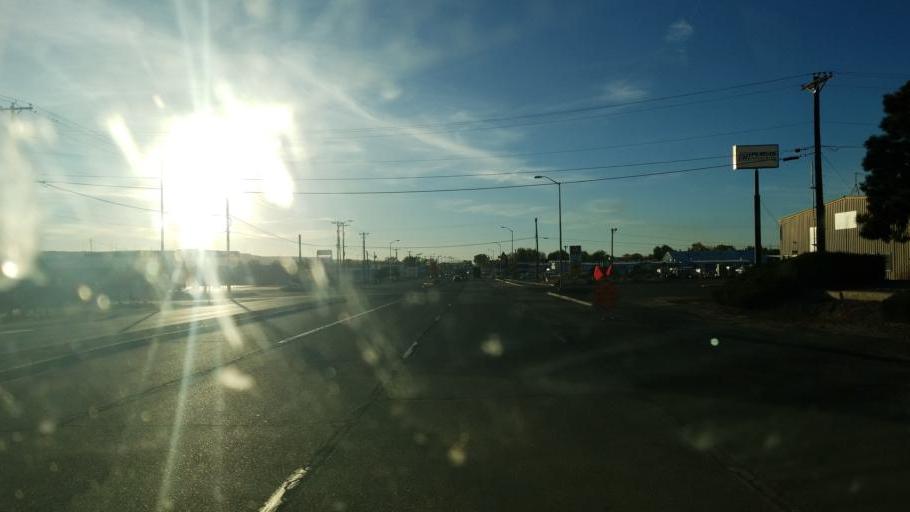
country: US
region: New Mexico
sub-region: San Juan County
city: Farmington
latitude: 36.7193
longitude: -108.1665
